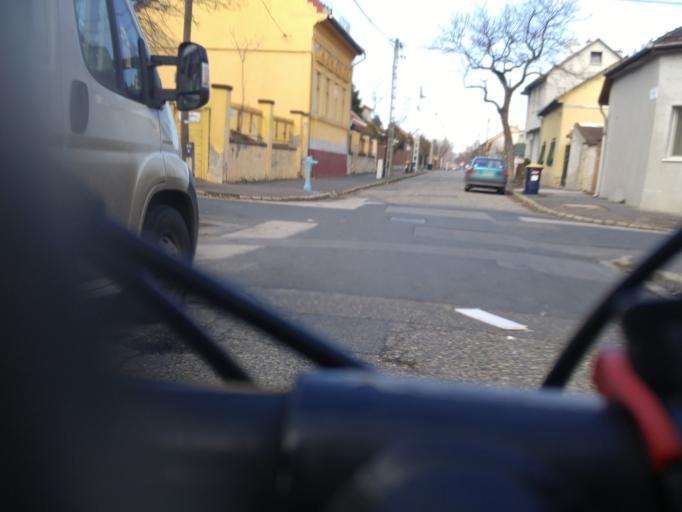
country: HU
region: Budapest
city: Budapest XX. keruelet
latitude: 47.4354
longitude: 19.1192
